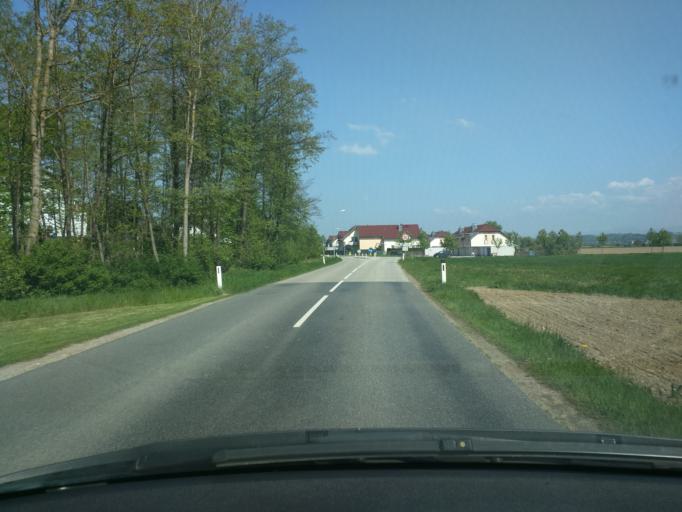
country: AT
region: Lower Austria
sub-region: Politischer Bezirk Amstetten
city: Sankt Georgen am Ybbsfelde
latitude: 48.1289
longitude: 14.9387
